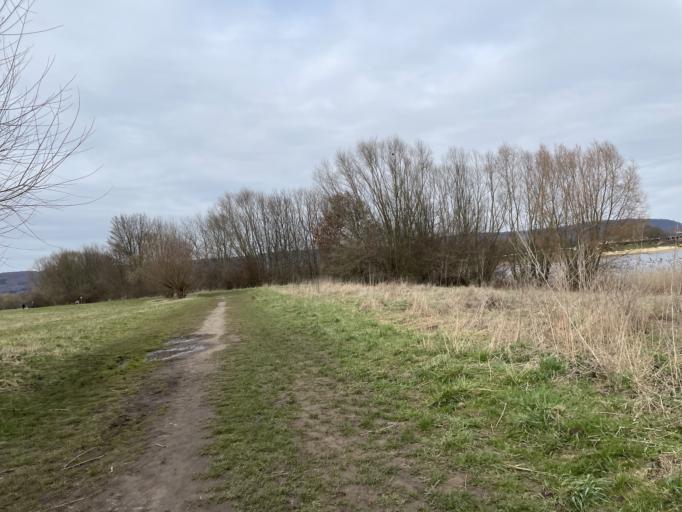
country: DE
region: North Rhine-Westphalia
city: Bad Oeynhausen
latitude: 52.2198
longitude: 8.8327
